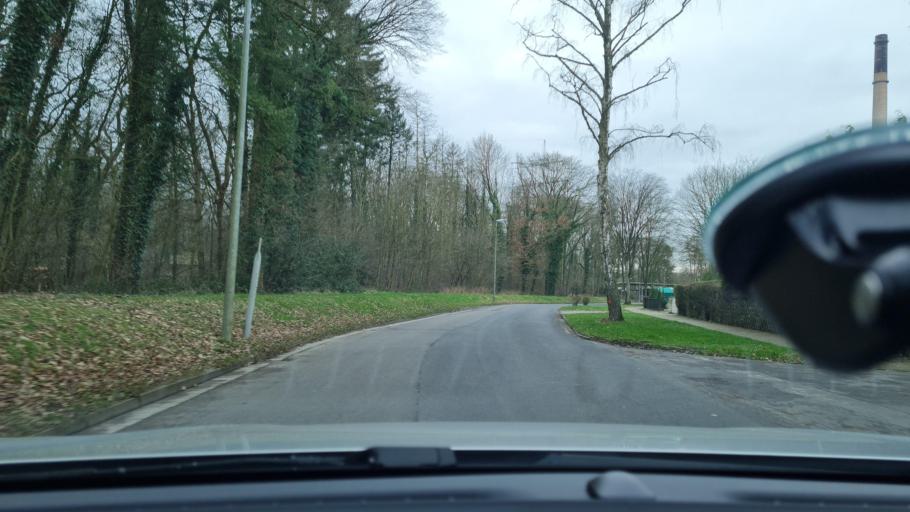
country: DE
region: North Rhine-Westphalia
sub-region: Regierungsbezirk Dusseldorf
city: Voerde
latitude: 51.5768
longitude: 6.6945
